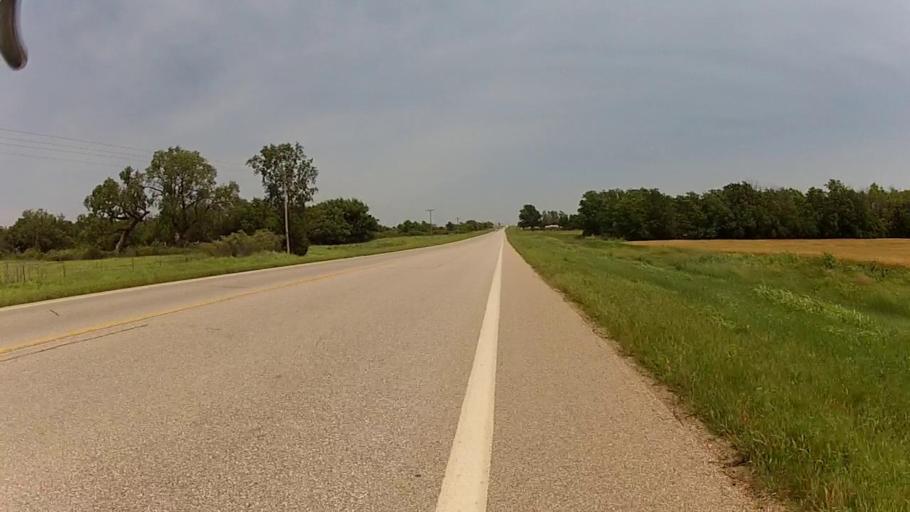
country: US
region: Kansas
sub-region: Cowley County
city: Arkansas City
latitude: 37.0563
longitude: -97.1184
